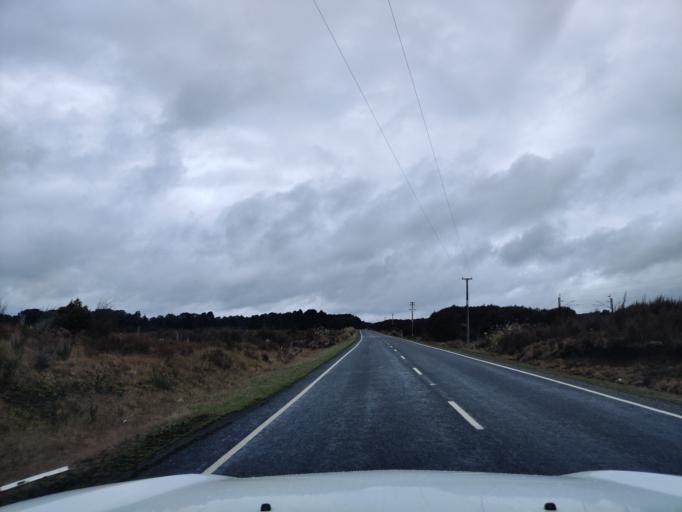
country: NZ
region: Manawatu-Wanganui
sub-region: Ruapehu District
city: Waiouru
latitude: -39.3400
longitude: 175.3785
